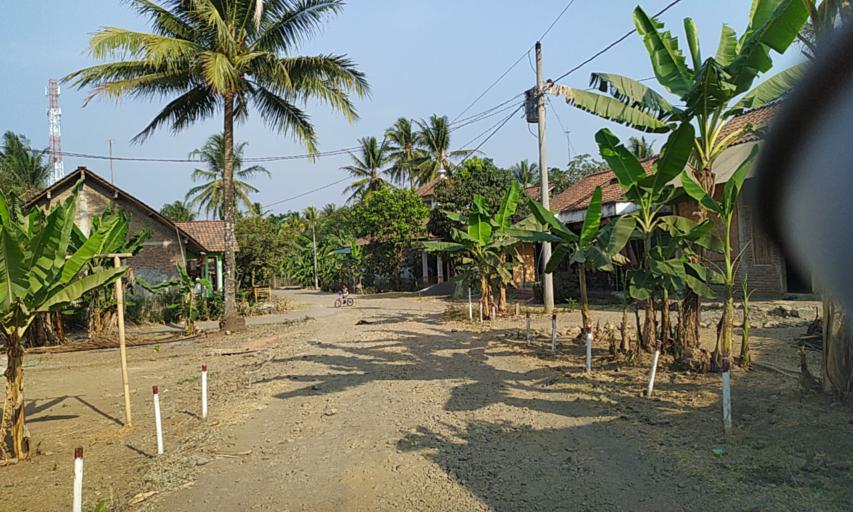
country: ID
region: Central Java
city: Padangsari
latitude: -7.3563
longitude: 108.7592
